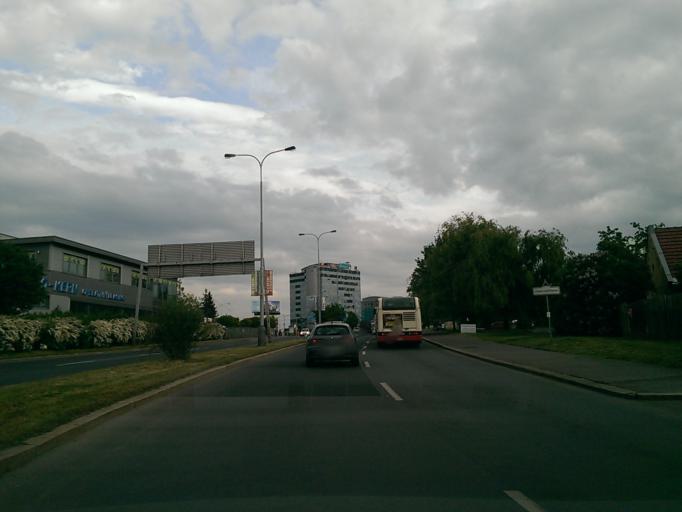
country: CZ
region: Central Bohemia
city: Vestec
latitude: 50.0405
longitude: 14.4898
